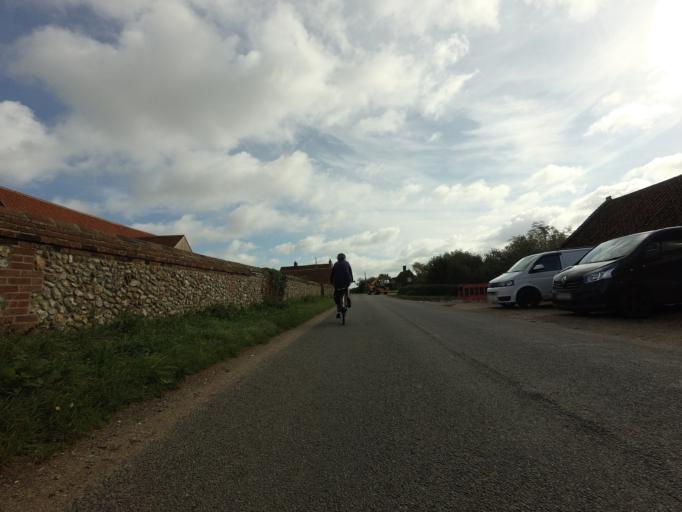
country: GB
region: England
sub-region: Norfolk
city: Wells-next-the-Sea
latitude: 52.9111
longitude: 0.7194
